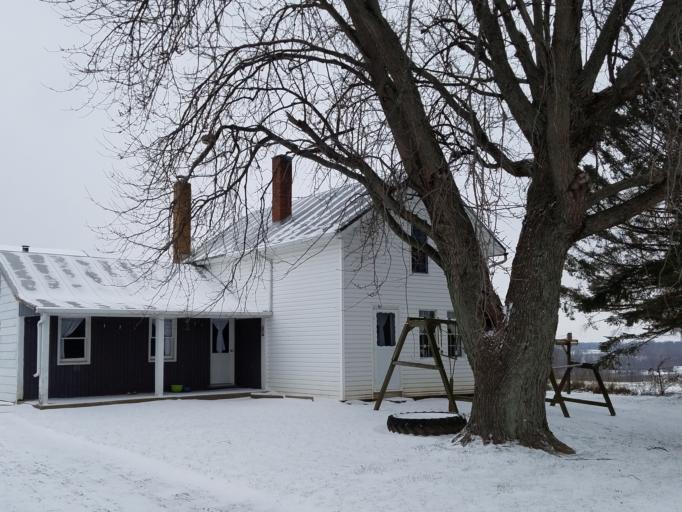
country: US
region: Ohio
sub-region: Knox County
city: Fredericktown
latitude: 40.5055
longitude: -82.6054
